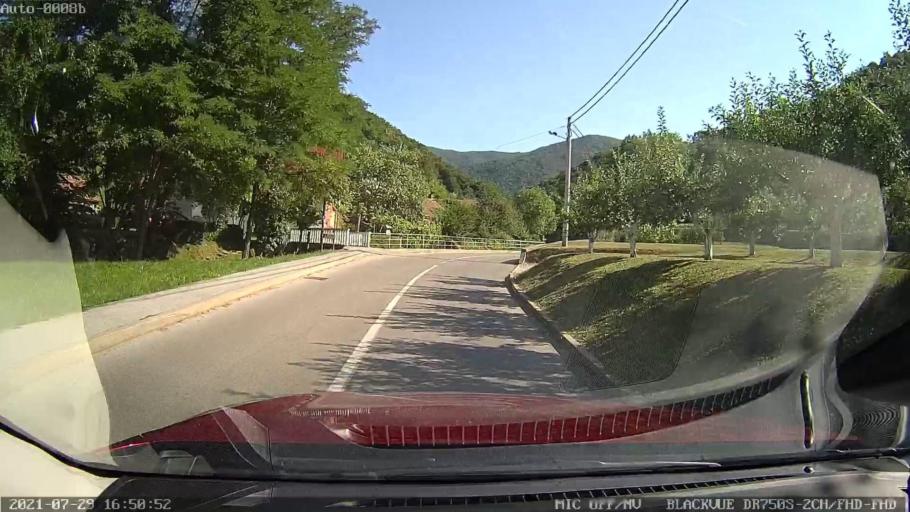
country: HR
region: Varazdinska
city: Ivanec
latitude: 46.2096
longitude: 16.1321
